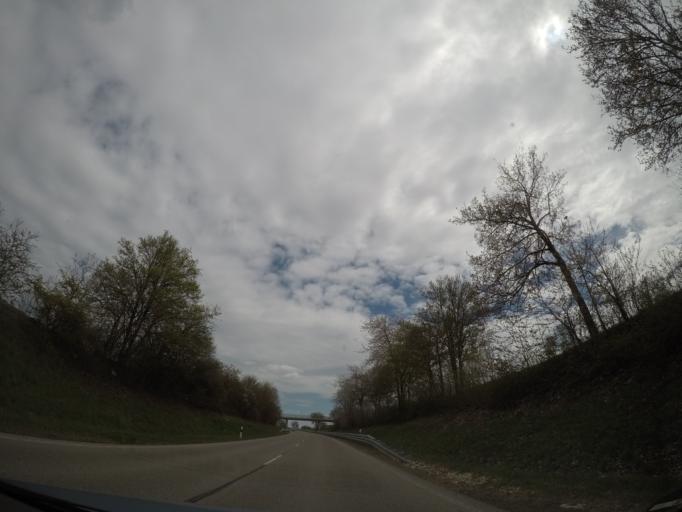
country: DE
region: Baden-Wuerttemberg
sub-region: Tuebingen Region
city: Laichingen
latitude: 48.4561
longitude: 9.7059
